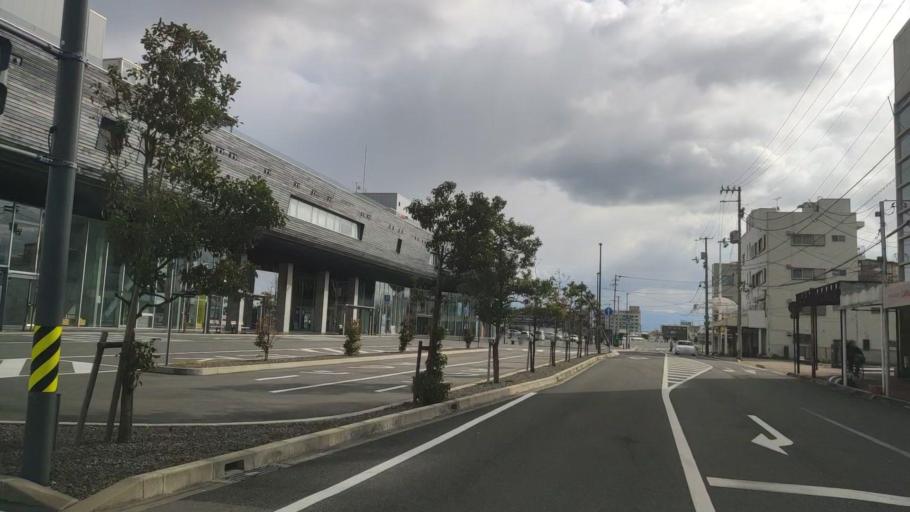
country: JP
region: Ehime
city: Saijo
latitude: 34.0700
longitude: 133.0044
